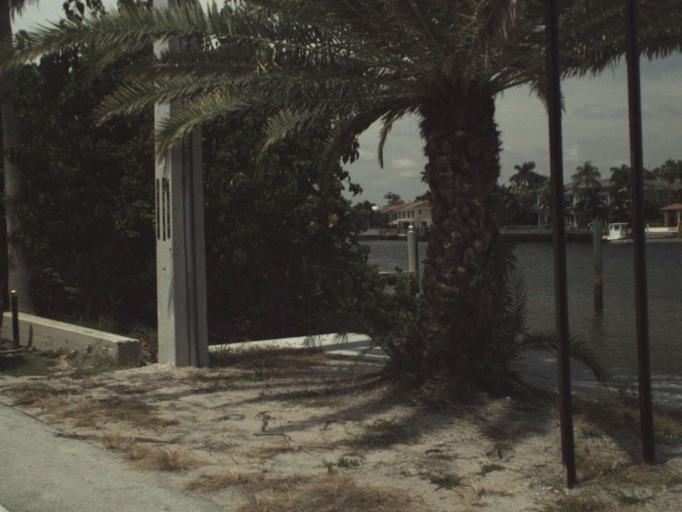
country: US
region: Florida
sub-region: Broward County
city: Lighthouse Point
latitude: 26.2644
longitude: -80.0814
